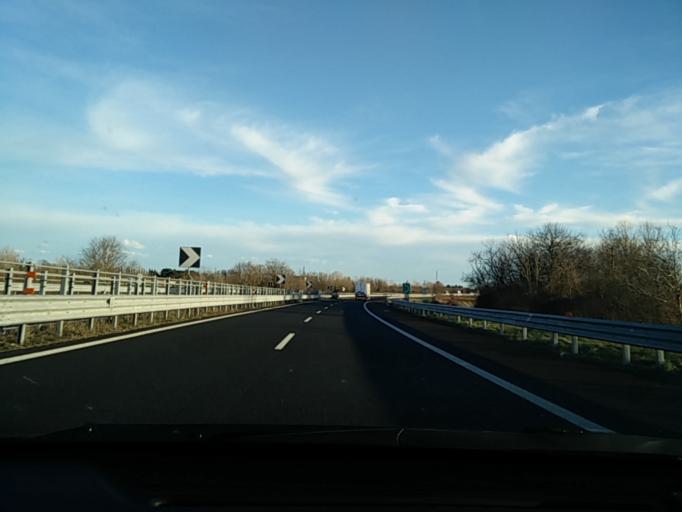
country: IT
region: Friuli Venezia Giulia
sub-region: Provincia di Udine
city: Pagnacco
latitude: 46.1253
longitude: 13.2030
